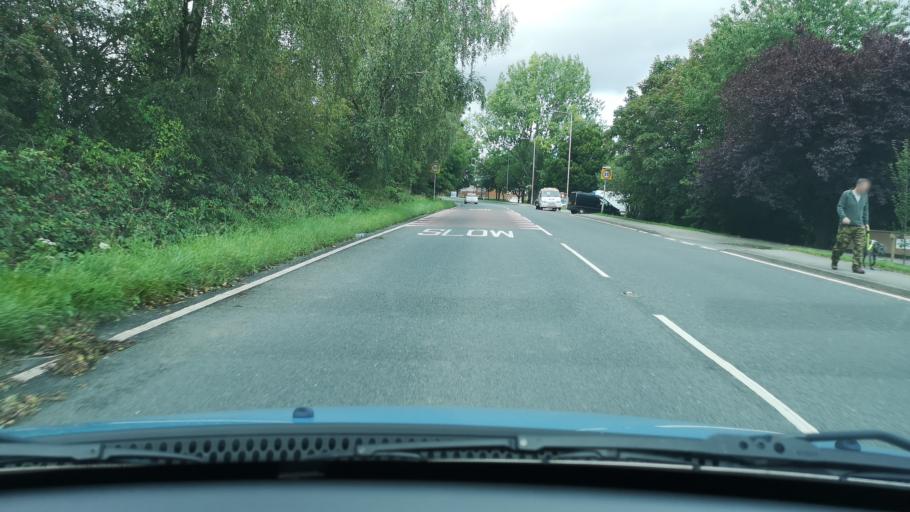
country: GB
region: England
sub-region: City and Borough of Wakefield
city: Low Ackworth
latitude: 53.6391
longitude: -1.3301
